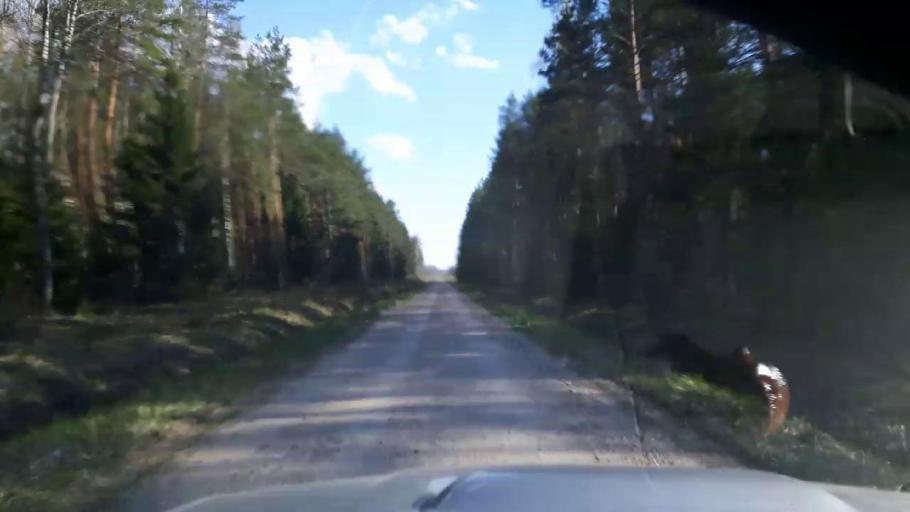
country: EE
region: Paernumaa
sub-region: Tootsi vald
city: Tootsi
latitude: 58.4224
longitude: 24.8517
